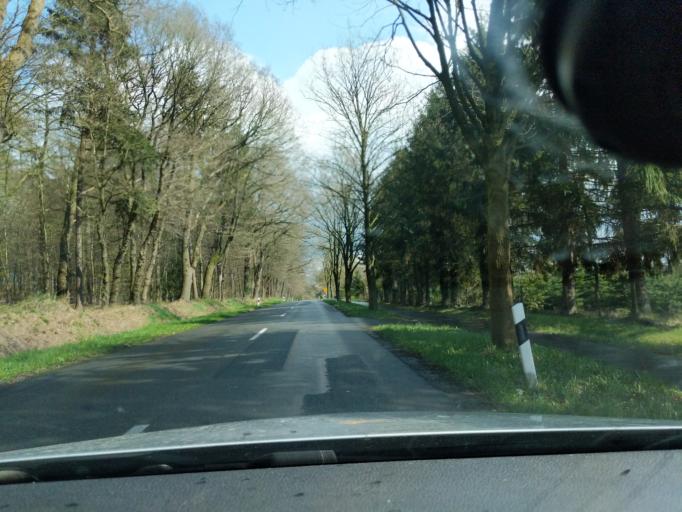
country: DE
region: Lower Saxony
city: Harsefeld
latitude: 53.4620
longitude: 9.4952
